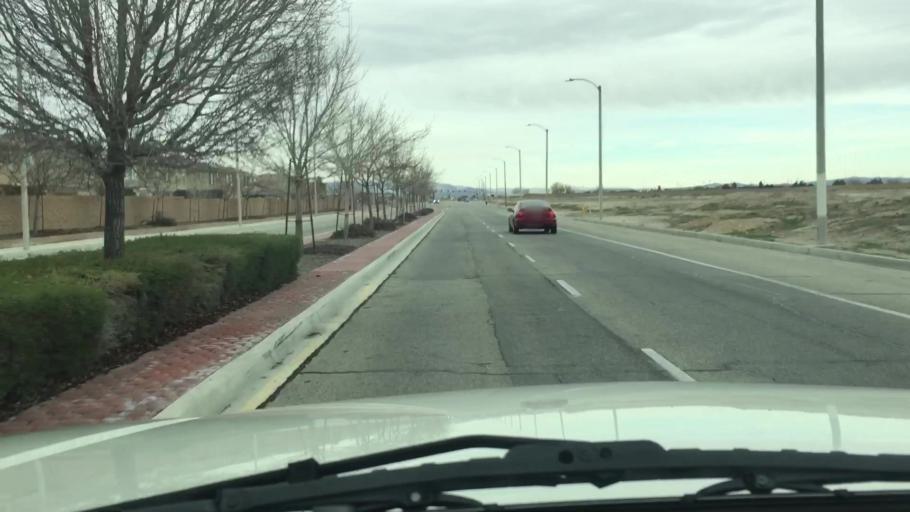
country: US
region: California
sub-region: Los Angeles County
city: Lancaster
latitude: 34.6986
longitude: -118.1838
